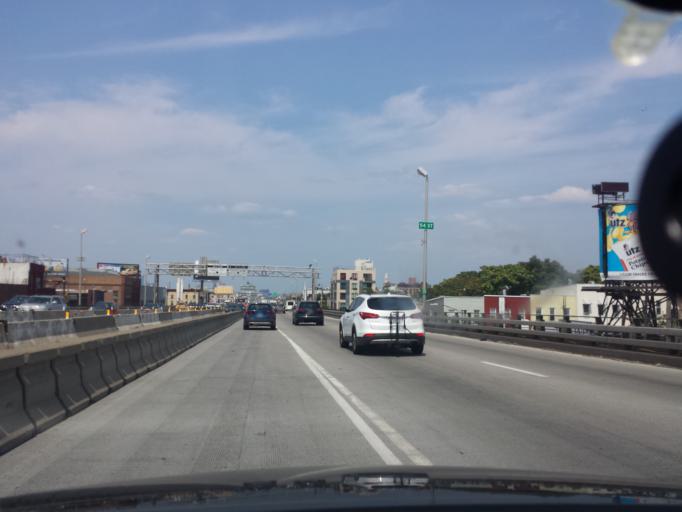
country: US
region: New York
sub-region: Kings County
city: Bensonhurst
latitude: 40.6450
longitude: -74.0173
